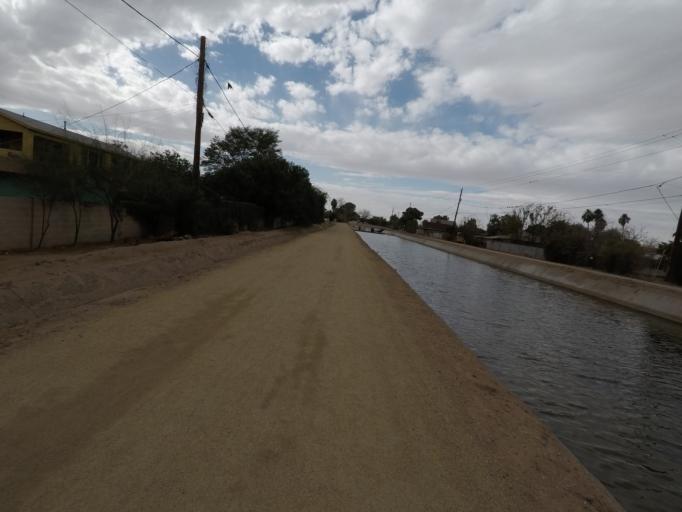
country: US
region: Arizona
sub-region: Maricopa County
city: Phoenix
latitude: 33.5007
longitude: -112.0895
